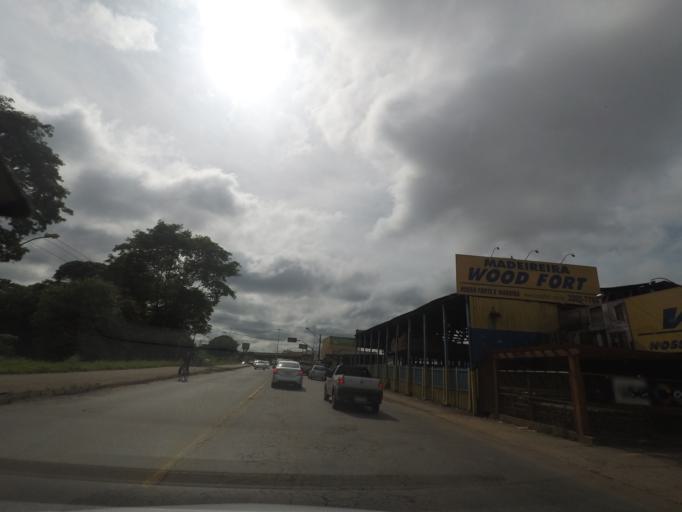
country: BR
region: Goias
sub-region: Goiania
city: Goiania
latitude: -16.7283
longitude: -49.2442
